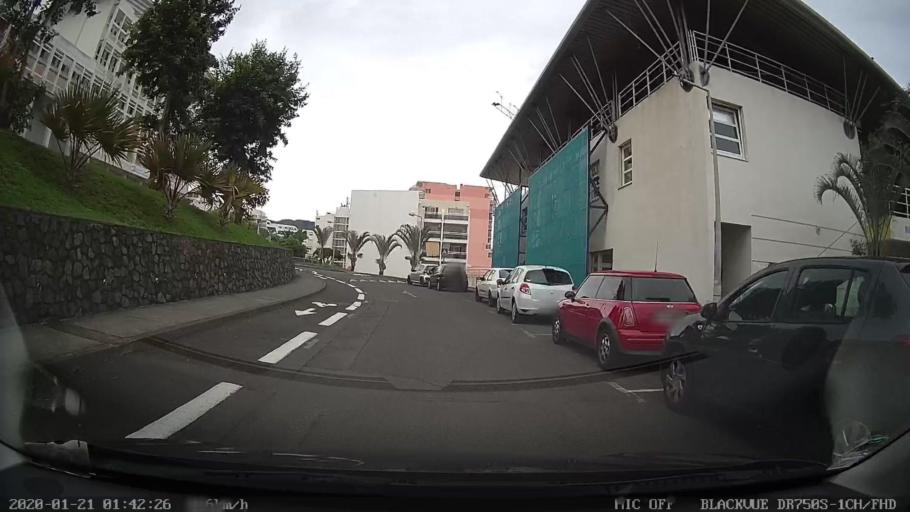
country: RE
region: Reunion
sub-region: Reunion
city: Saint-Denis
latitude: -20.9017
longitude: 55.4831
